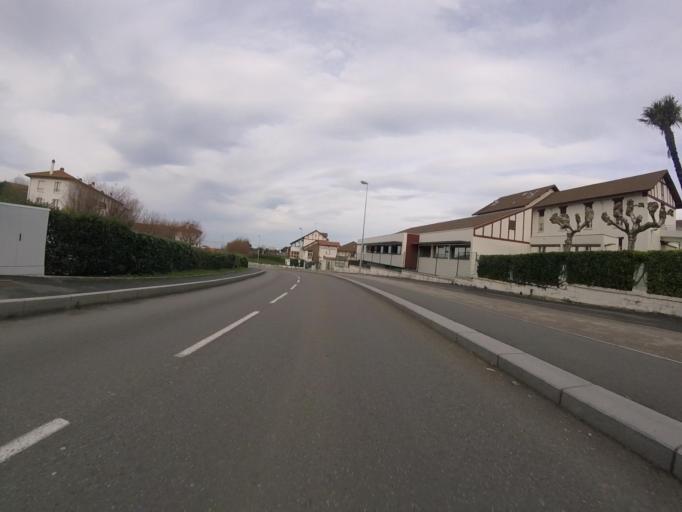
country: FR
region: Aquitaine
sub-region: Departement des Pyrenees-Atlantiques
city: Hendaye
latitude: 43.3744
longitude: -1.7605
